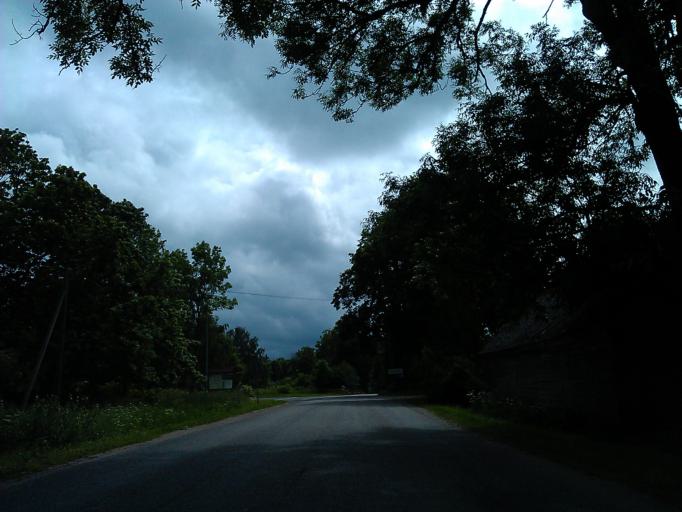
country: LV
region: Aizpute
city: Aizpute
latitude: 56.7266
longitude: 21.6071
